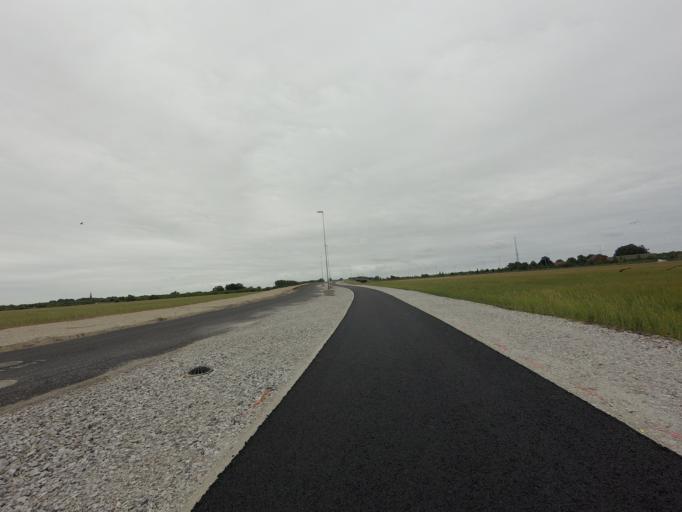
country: SE
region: Skane
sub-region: Malmo
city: Bunkeflostrand
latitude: 55.5617
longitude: 12.9441
